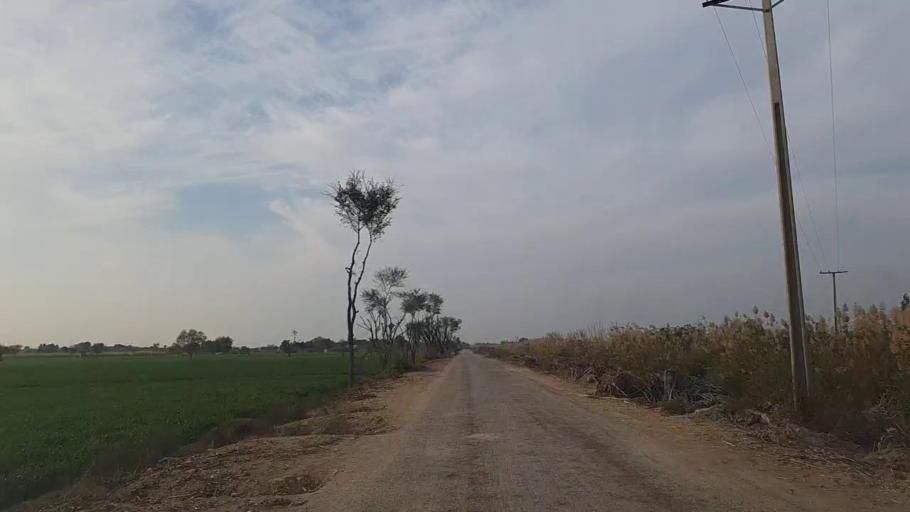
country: PK
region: Sindh
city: Daur
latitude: 26.4992
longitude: 68.4468
